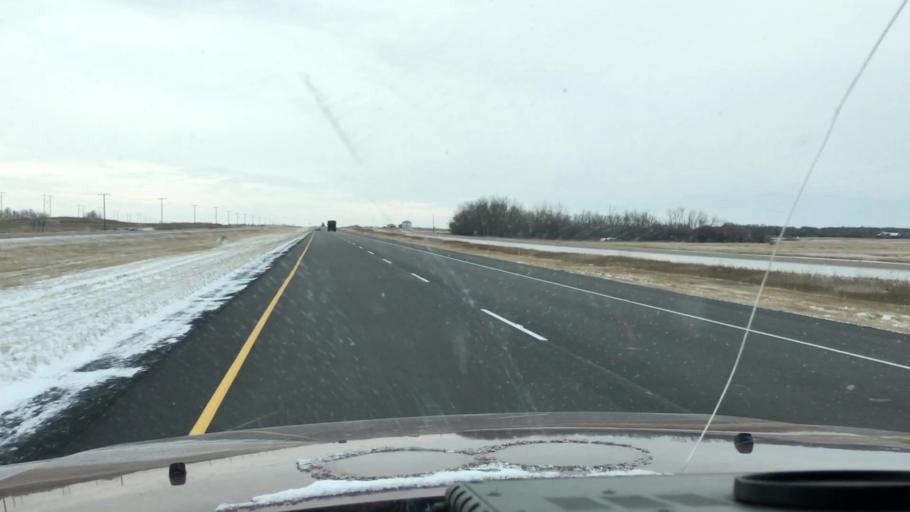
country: CA
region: Saskatchewan
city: Saskatoon
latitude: 51.9372
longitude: -106.5387
